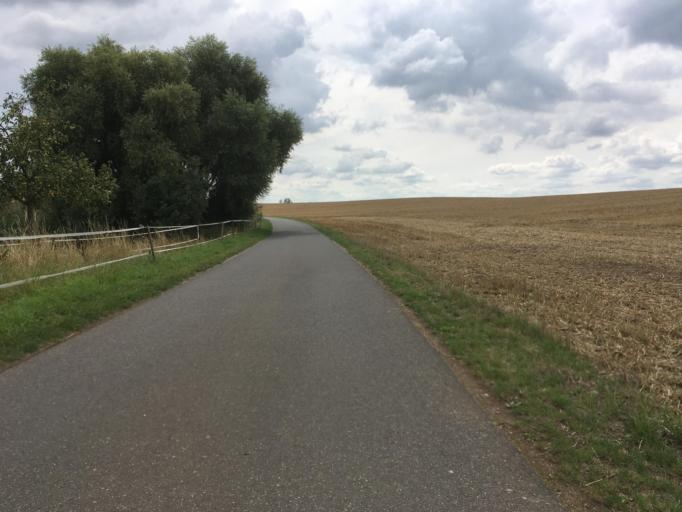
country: DE
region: Brandenburg
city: Prenzlau
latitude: 53.2665
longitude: 13.8937
